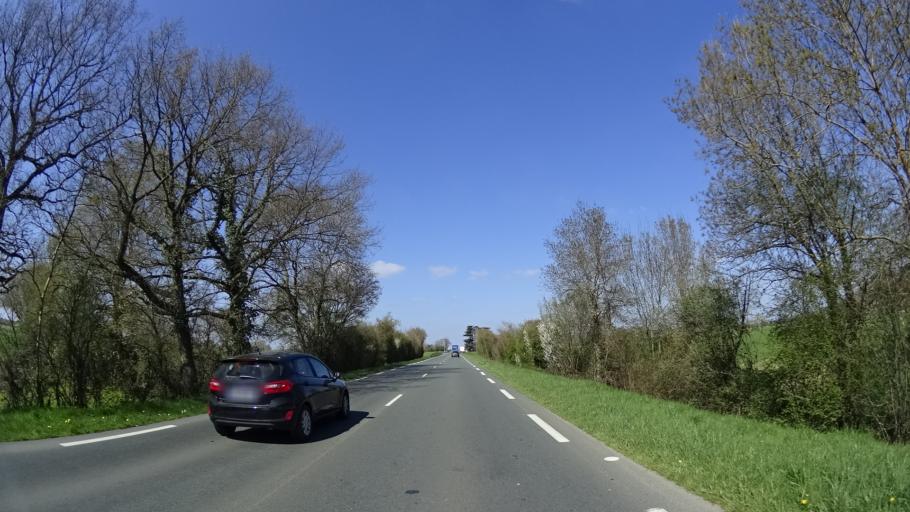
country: FR
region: Pays de la Loire
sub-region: Departement de Maine-et-Loire
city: Brissac-Quince
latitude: 47.3300
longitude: -0.4213
